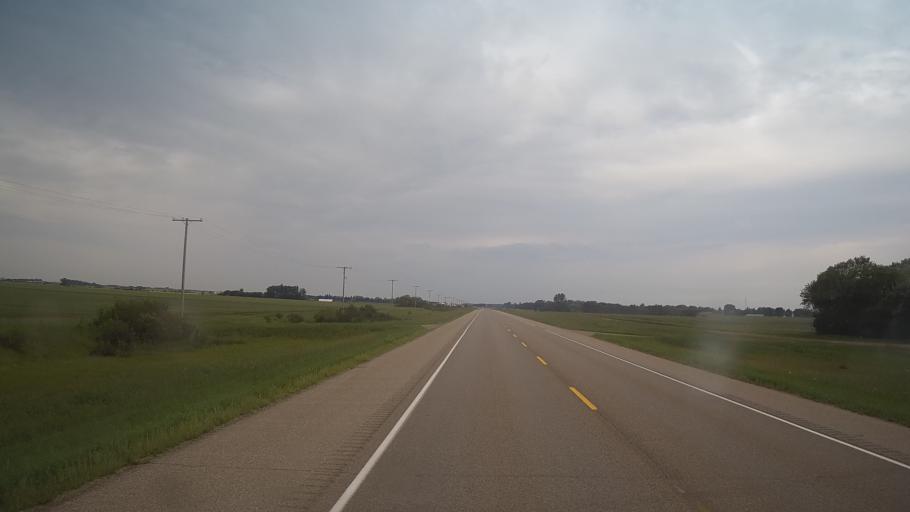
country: CA
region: Saskatchewan
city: Langham
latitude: 52.1288
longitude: -107.2019
